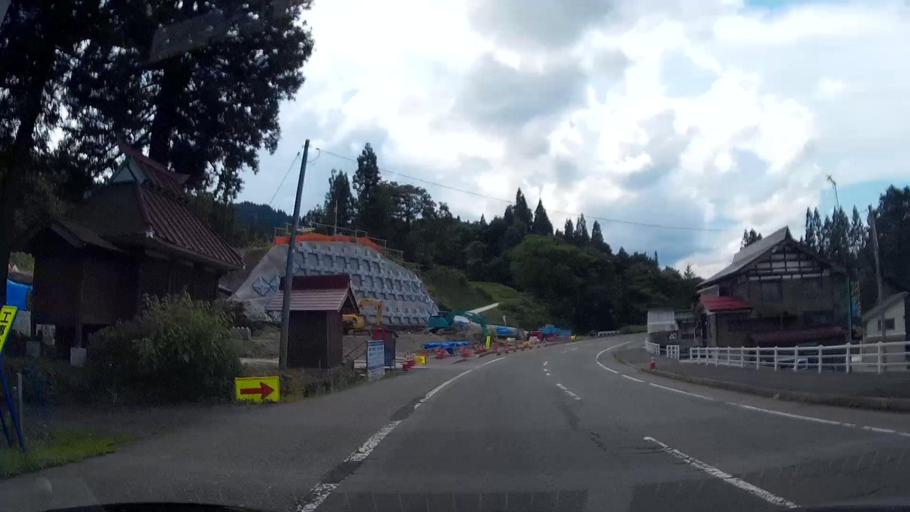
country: JP
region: Niigata
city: Tokamachi
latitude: 36.9950
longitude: 138.6153
